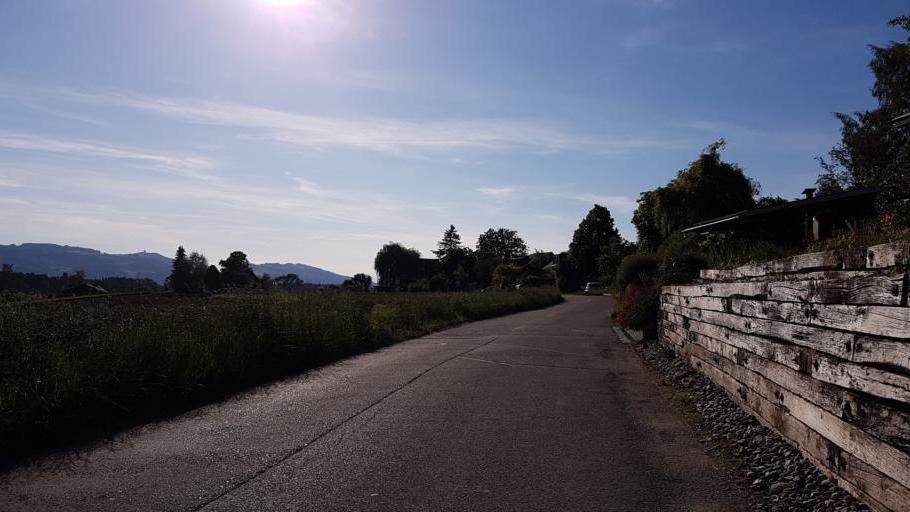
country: CH
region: Bern
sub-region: Bern-Mittelland District
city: Worb
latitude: 46.9041
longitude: 7.5749
